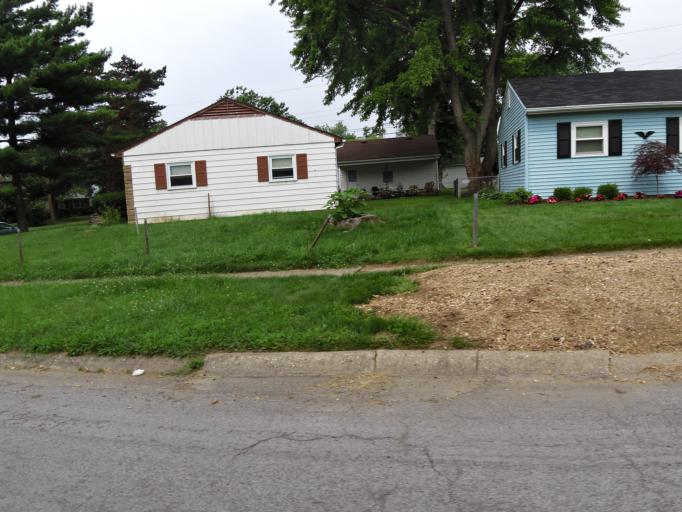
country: US
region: Ohio
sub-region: Montgomery County
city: Riverside
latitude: 39.7343
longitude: -84.1230
